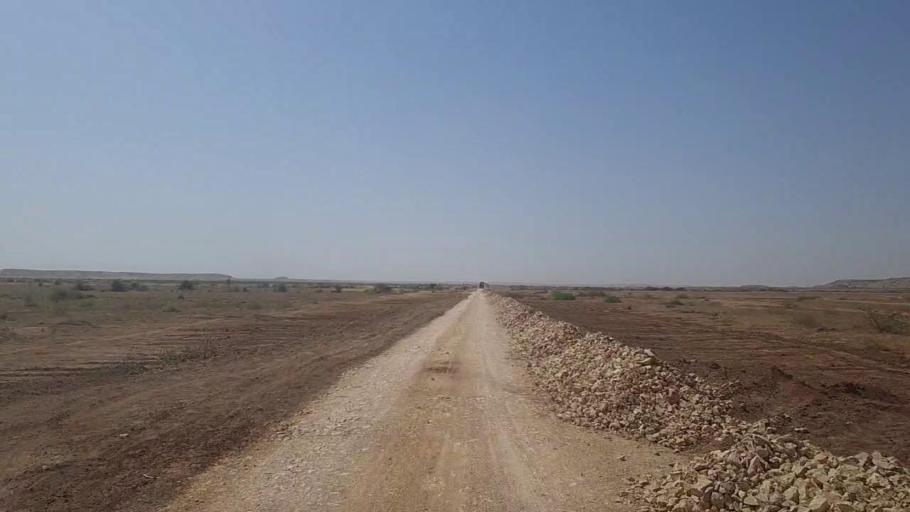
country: PK
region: Sindh
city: Kotri
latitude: 25.1468
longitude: 68.1877
